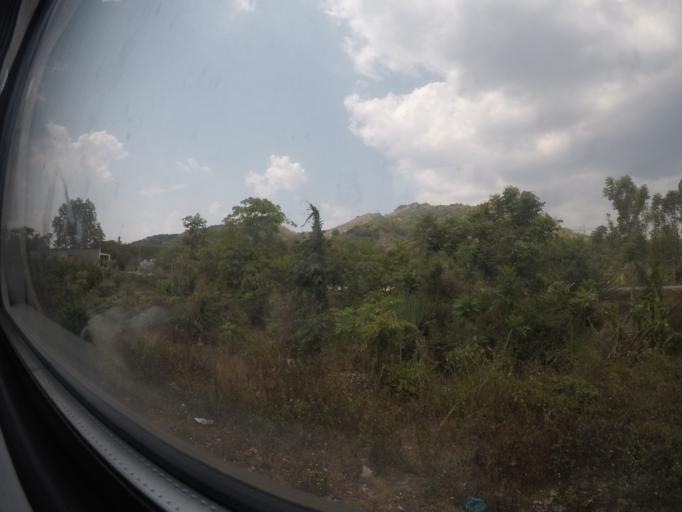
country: VN
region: Binh Thuan
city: Tanh Linh
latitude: 10.9707
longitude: 107.6276
